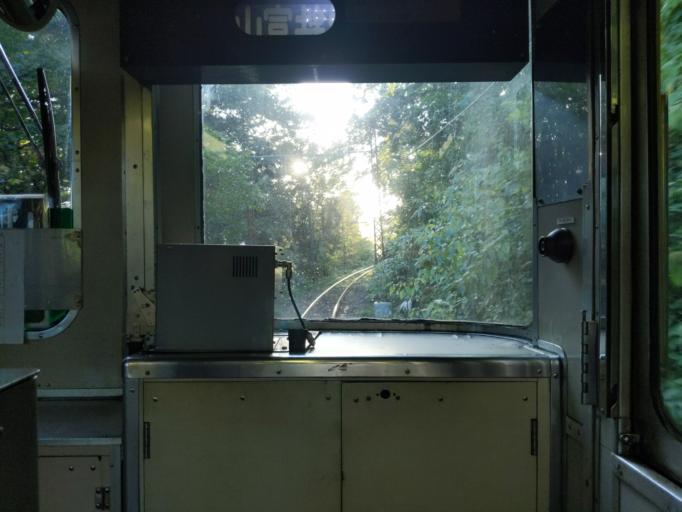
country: JP
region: Toyama
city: Kamiichi
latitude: 36.5745
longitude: 137.3658
